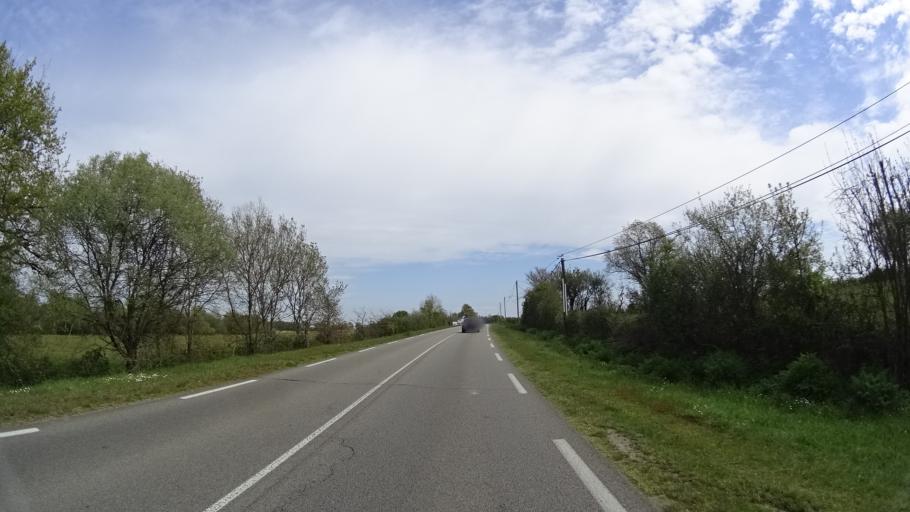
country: FR
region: Pays de la Loire
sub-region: Departement de la Loire-Atlantique
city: Sainte-Pazanne
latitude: 47.1101
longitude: -1.7845
